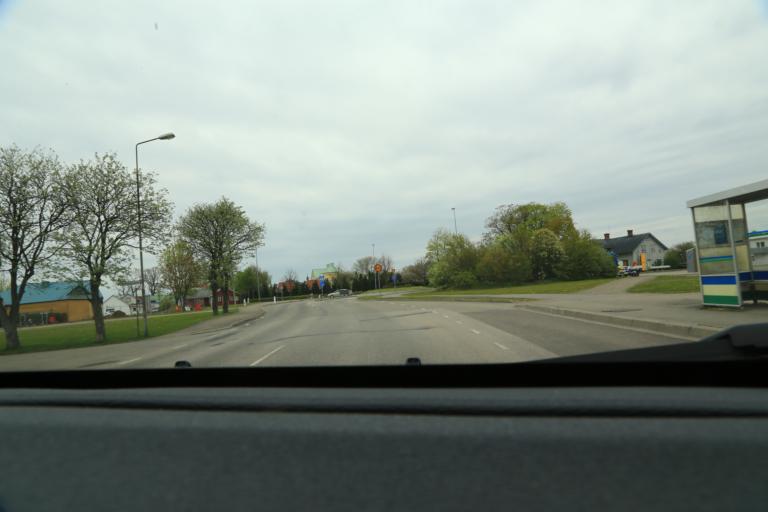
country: SE
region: Halland
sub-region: Varbergs Kommun
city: Tvaaker
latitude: 57.0415
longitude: 12.3986
